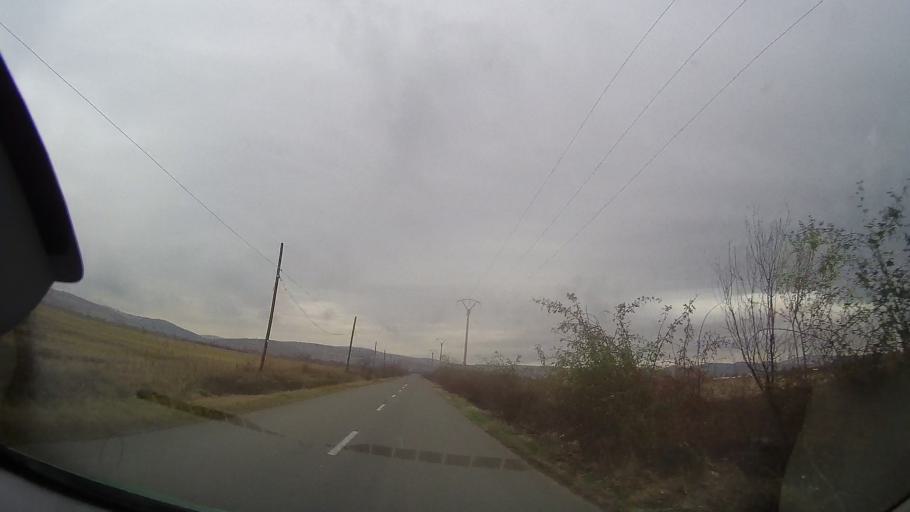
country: RO
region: Prahova
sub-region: Comuna Fantanele
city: Fantanele
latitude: 45.0185
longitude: 26.3804
